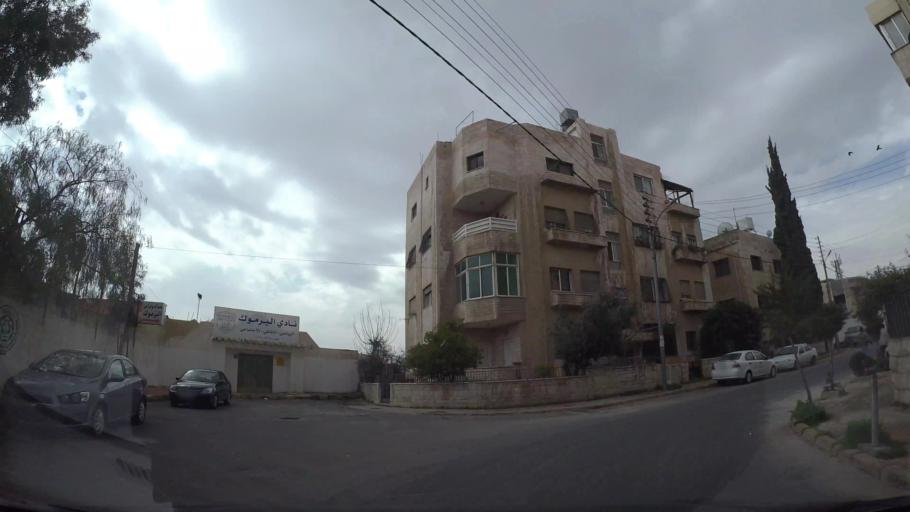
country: JO
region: Amman
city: Amman
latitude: 31.9811
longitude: 35.9213
